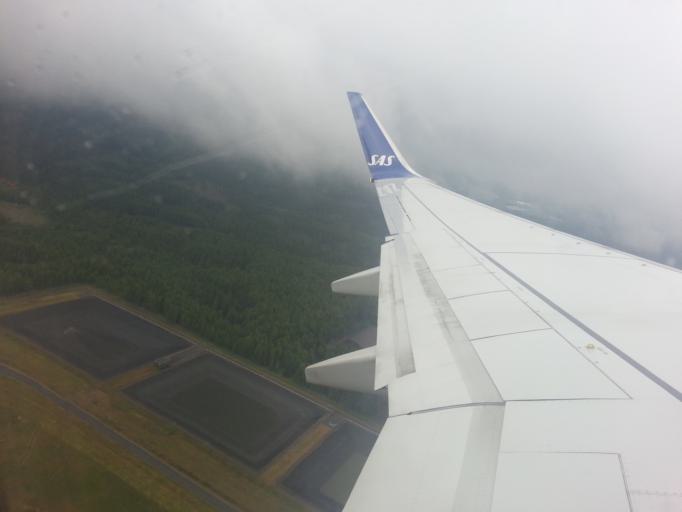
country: NO
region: Akershus
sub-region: Ullensaker
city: Jessheim
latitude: 60.1704
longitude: 11.1048
